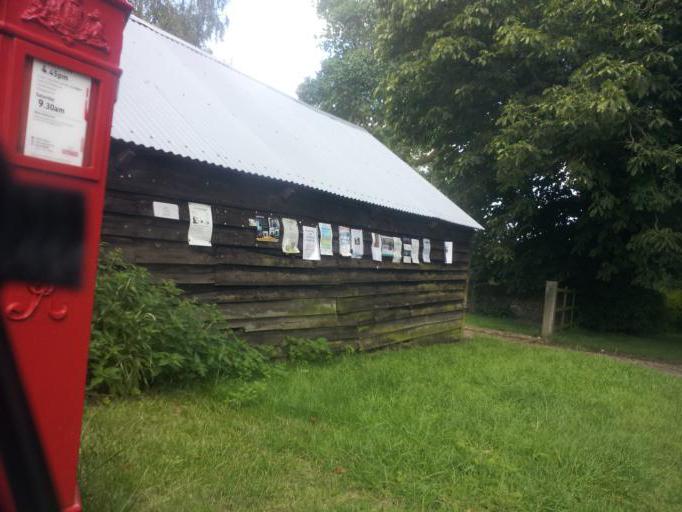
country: GB
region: England
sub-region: Kent
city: Harrietsham
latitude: 51.2845
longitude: 0.6955
